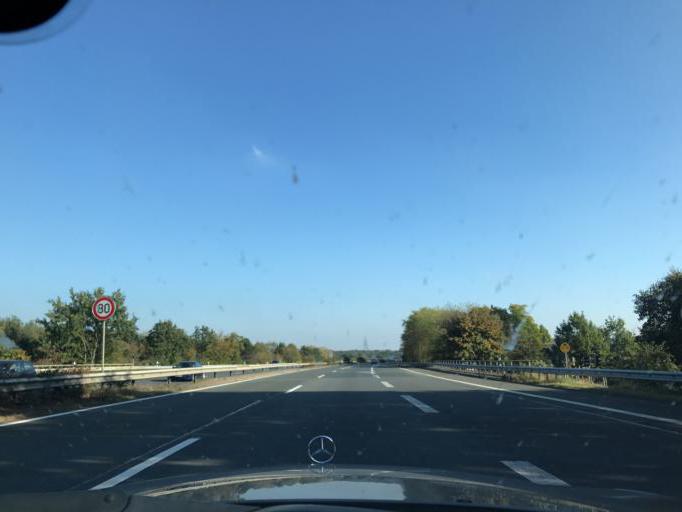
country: DE
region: Lower Saxony
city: Oldenburg
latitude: 53.1576
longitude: 8.1686
